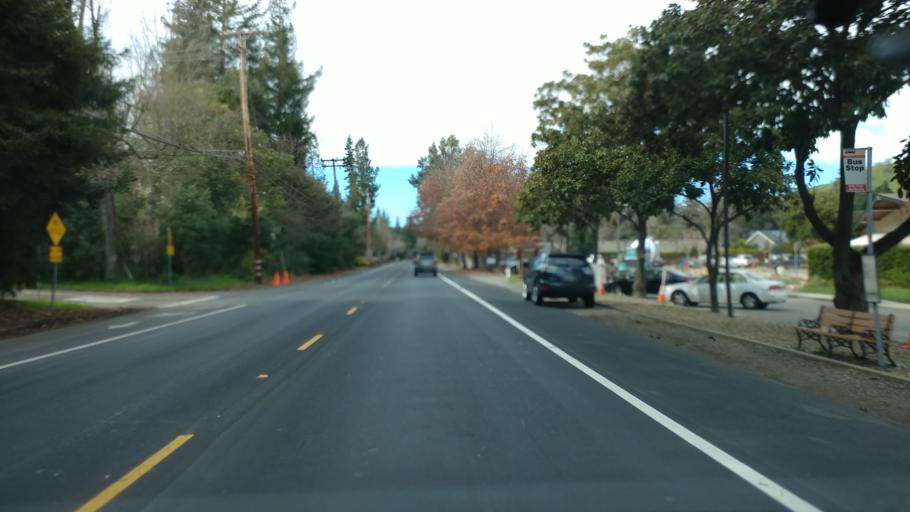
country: US
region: California
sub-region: Contra Costa County
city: Alamo
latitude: 37.8349
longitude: -122.0170
